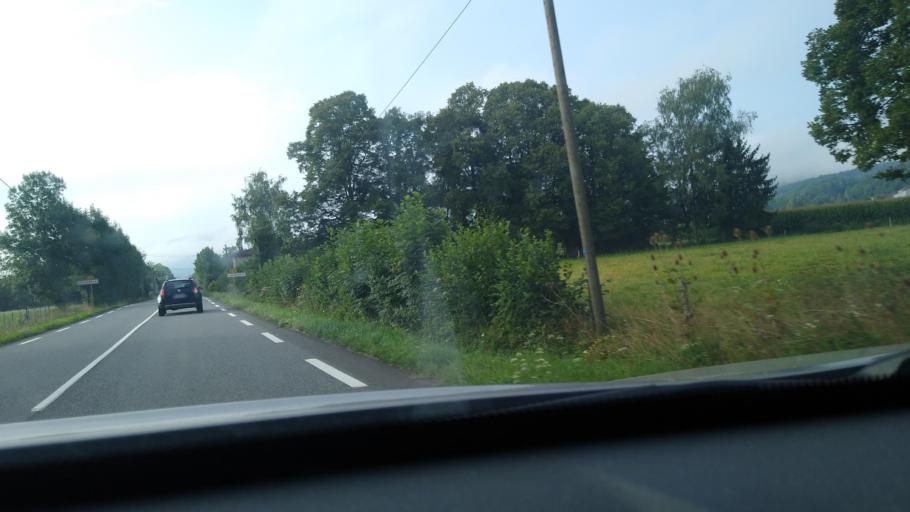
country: FR
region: Midi-Pyrenees
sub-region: Departement de la Haute-Garonne
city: Salies-du-Salat
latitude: 43.0596
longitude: 0.9752
